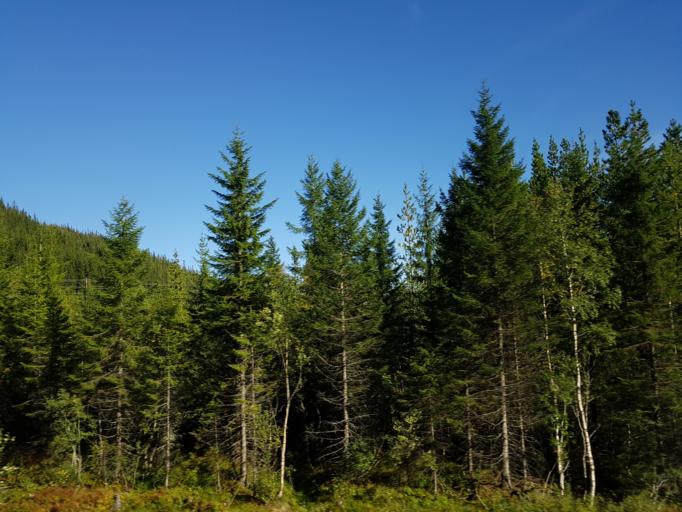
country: NO
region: Sor-Trondelag
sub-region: Afjord
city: A i Afjord
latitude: 63.6928
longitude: 10.2442
